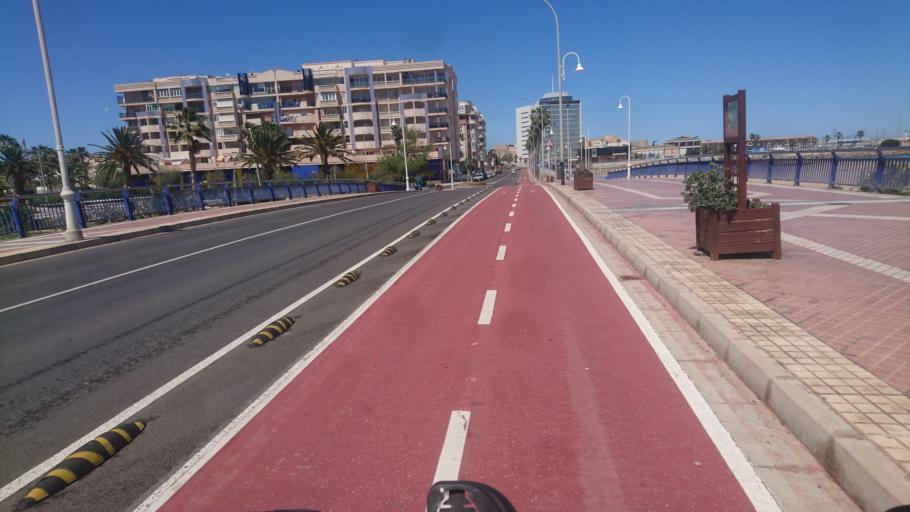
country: ES
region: Melilla
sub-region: Melilla
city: Melilla
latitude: 35.2857
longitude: -2.9385
